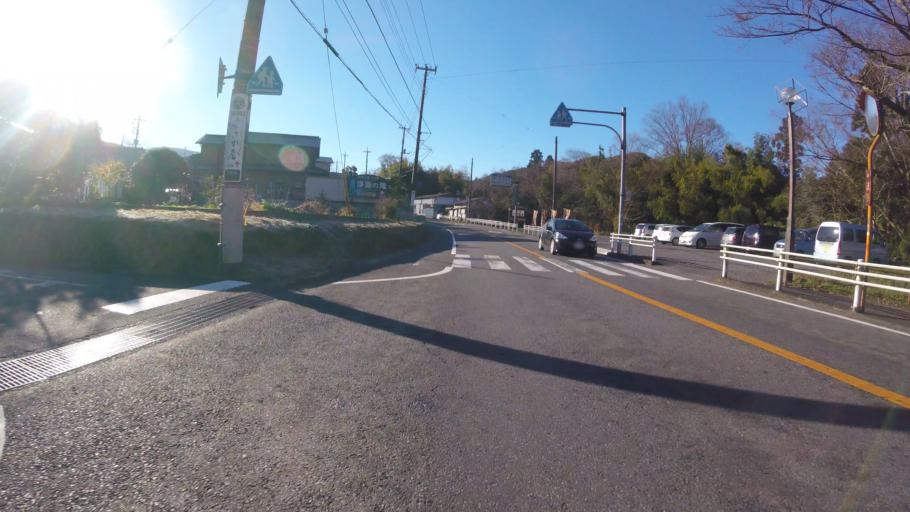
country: JP
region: Shizuoka
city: Heda
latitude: 34.9114
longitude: 138.9240
